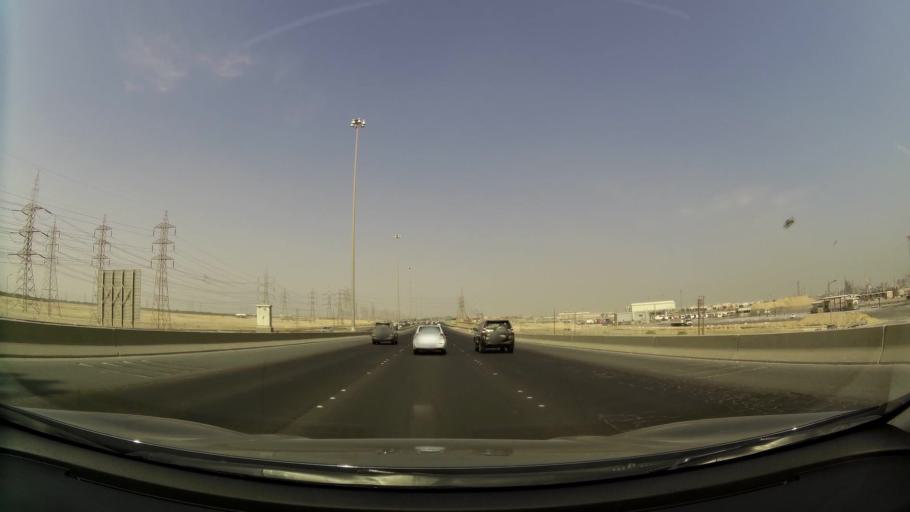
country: KW
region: Al Ahmadi
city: Al Fahahil
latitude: 29.0490
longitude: 48.1126
